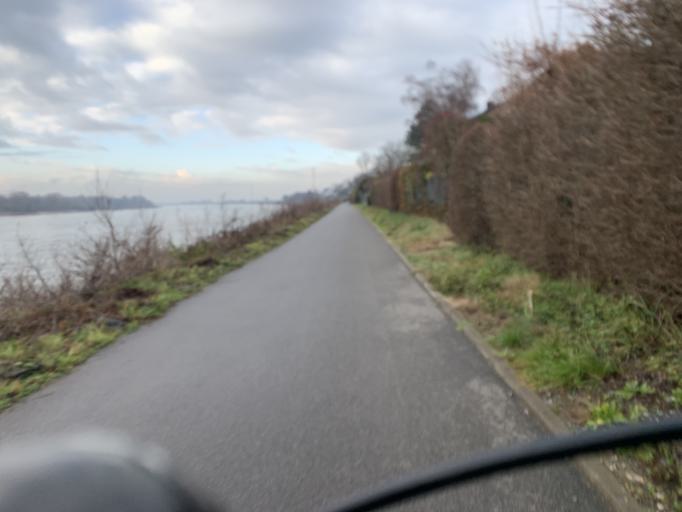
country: DE
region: North Rhine-Westphalia
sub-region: Regierungsbezirk Dusseldorf
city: Meerbusch
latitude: 51.3265
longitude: 6.7305
